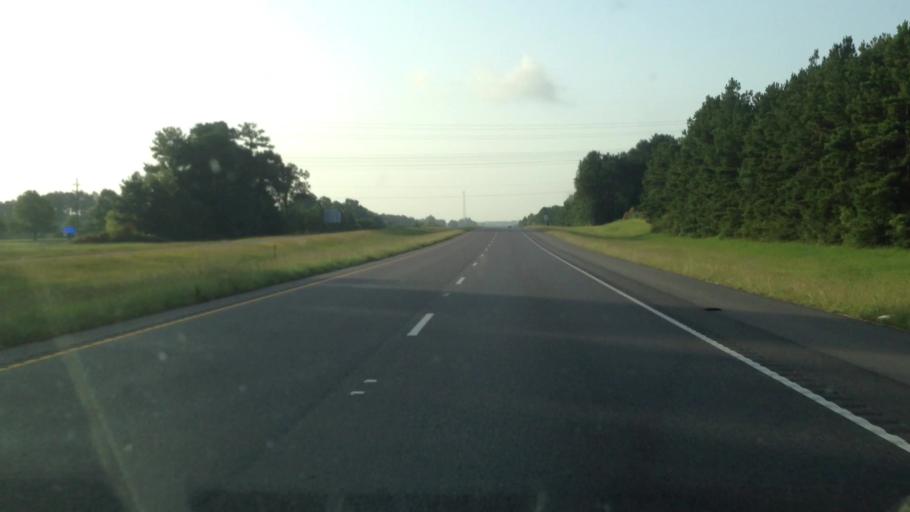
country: US
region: Louisiana
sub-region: Rapides Parish
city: Boyce
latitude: 31.4039
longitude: -92.7091
